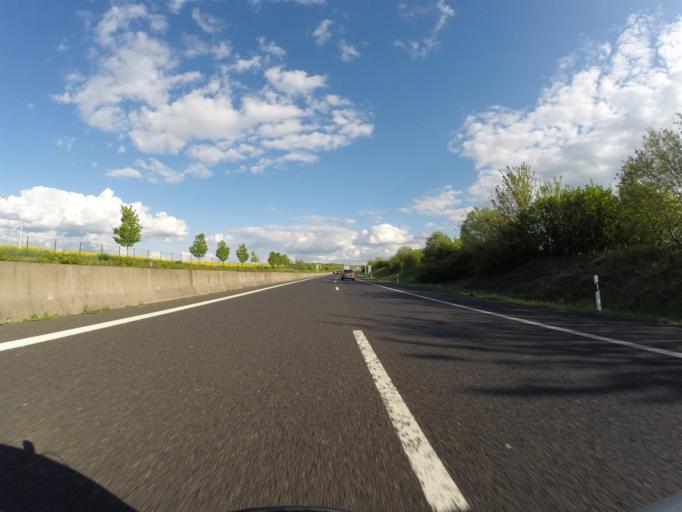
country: LU
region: Grevenmacher
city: Schengen
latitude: 49.4899
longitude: 6.3303
